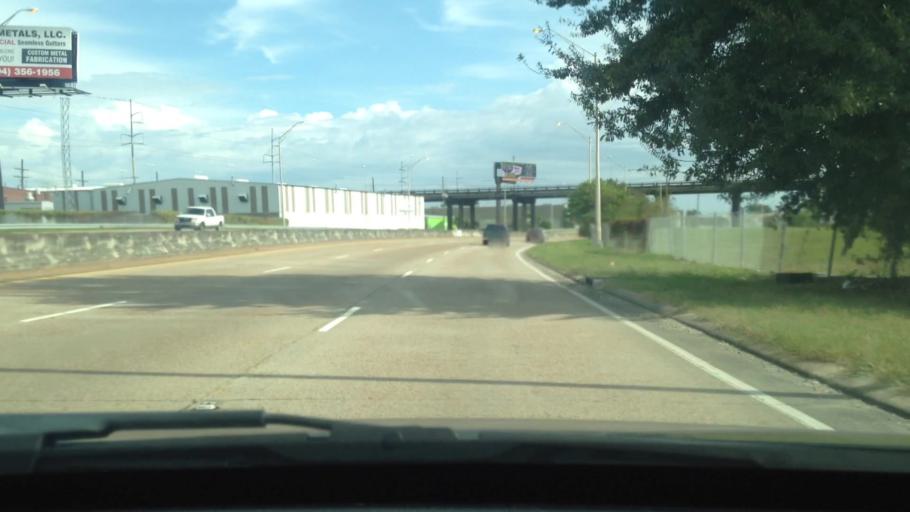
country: US
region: Louisiana
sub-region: Jefferson Parish
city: Jefferson
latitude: 29.9714
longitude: -90.1586
